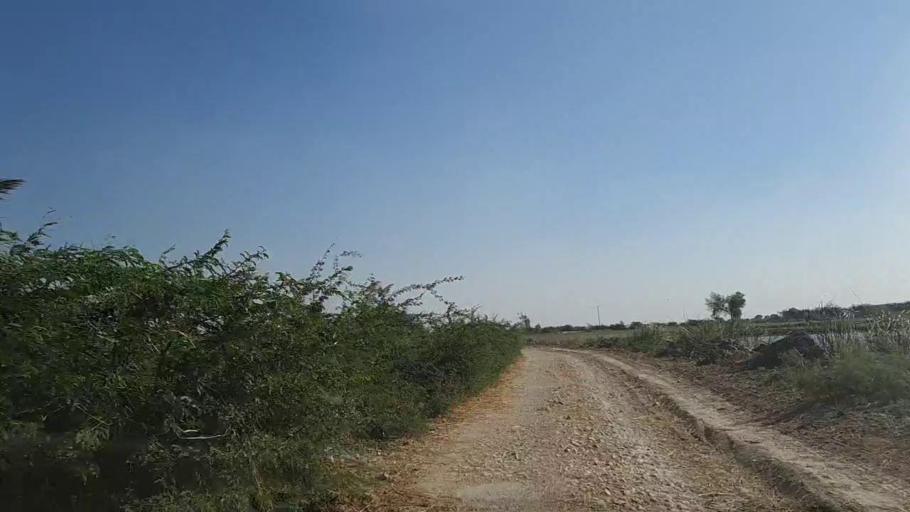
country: PK
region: Sindh
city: Daro Mehar
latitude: 24.7509
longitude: 68.0637
